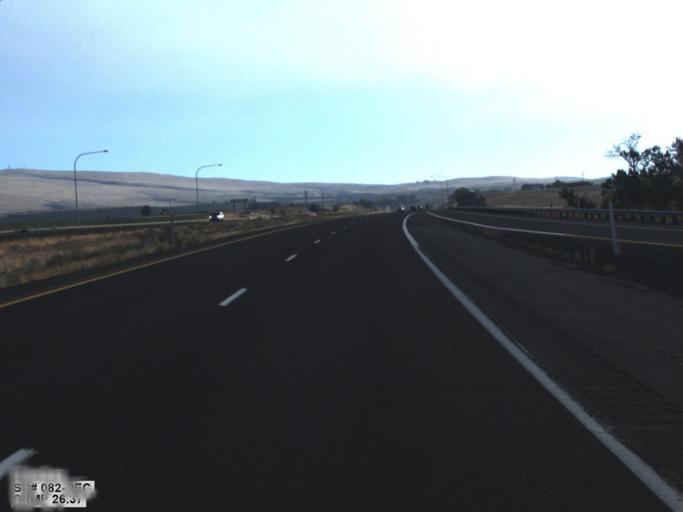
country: US
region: Washington
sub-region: Yakima County
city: Selah
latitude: 46.6796
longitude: -120.4781
